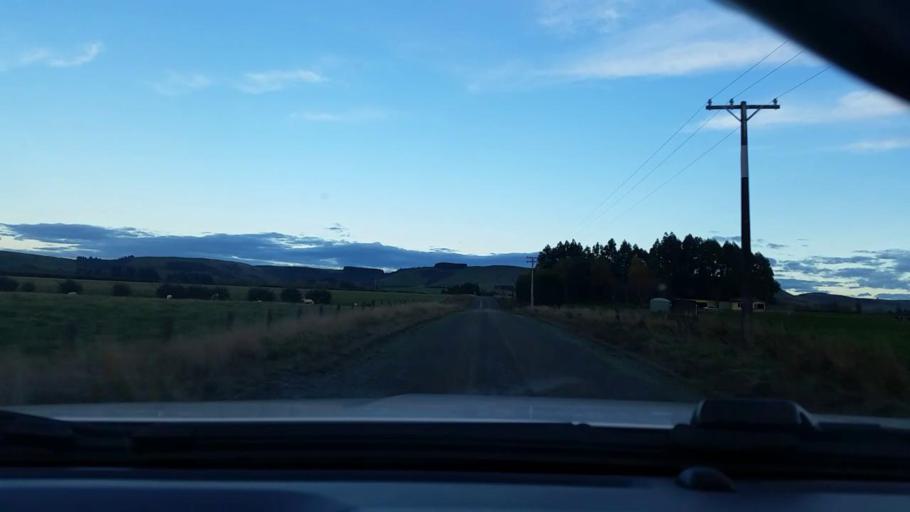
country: NZ
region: Southland
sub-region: Southland District
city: Winton
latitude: -46.1086
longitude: 168.4416
